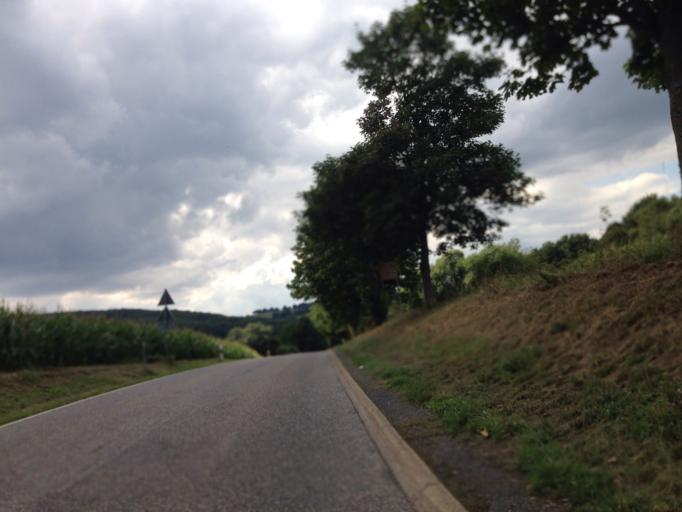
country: DE
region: Hesse
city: Merenberg
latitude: 50.5464
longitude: 8.2103
